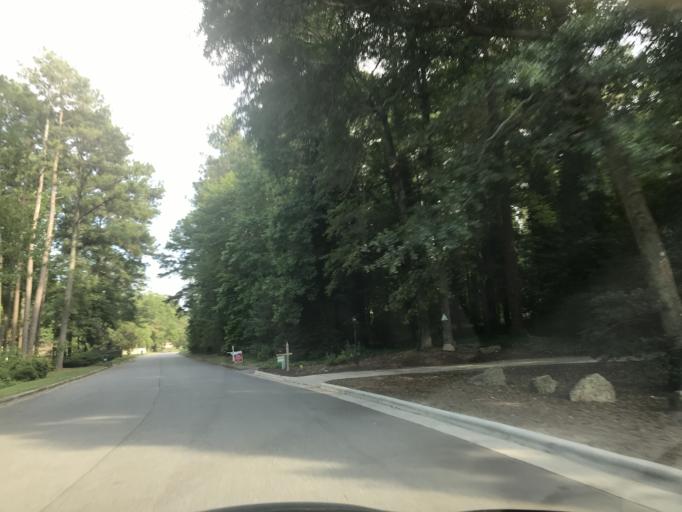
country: US
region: North Carolina
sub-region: Wake County
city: Knightdale
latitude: 35.8272
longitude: -78.5476
